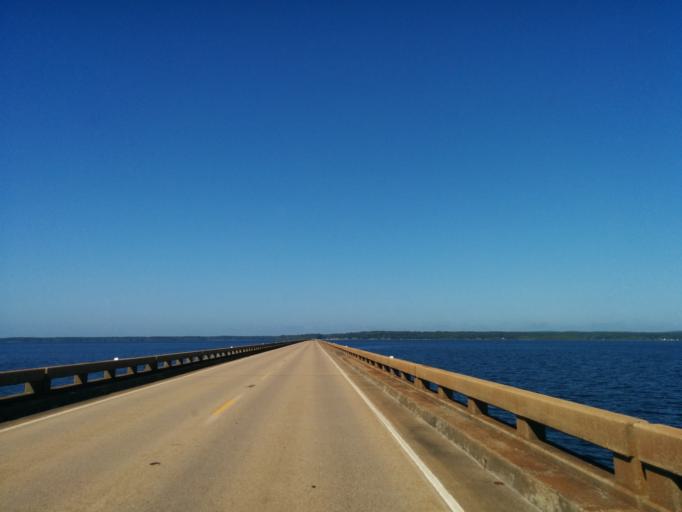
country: US
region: Texas
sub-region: Sabine County
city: Milam
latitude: 31.4828
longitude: -93.7186
